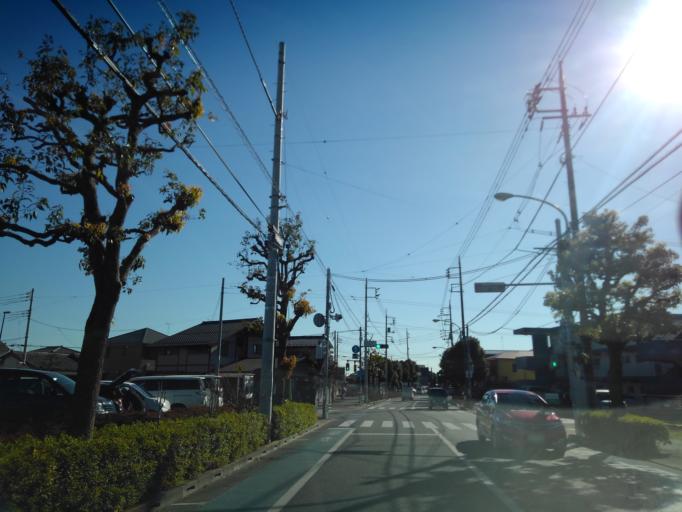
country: JP
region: Tokyo
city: Fussa
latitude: 35.7672
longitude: 139.3074
